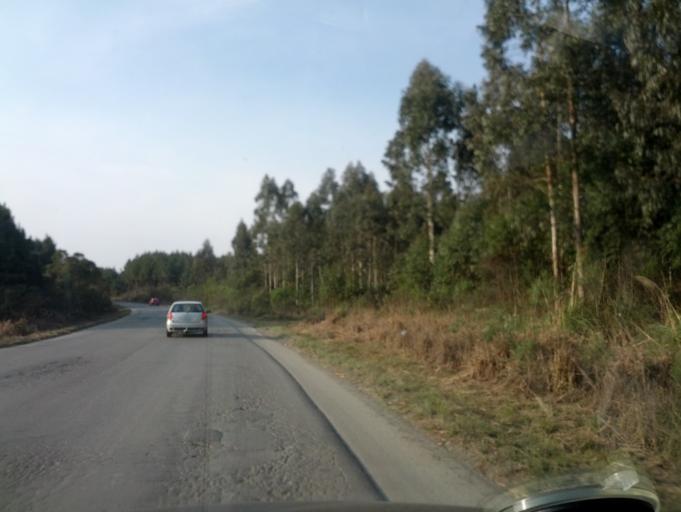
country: BR
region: Santa Catarina
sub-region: Otacilio Costa
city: Otacilio Costa
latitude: -27.5676
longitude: -50.1507
